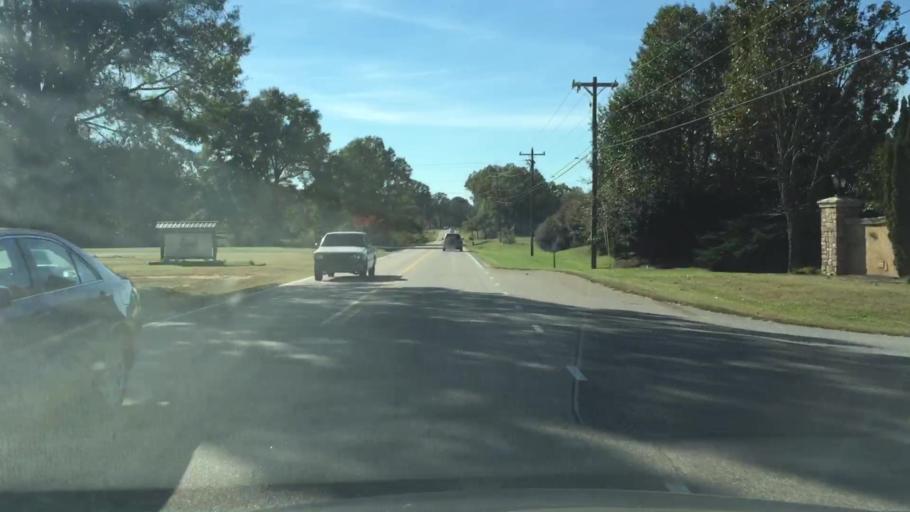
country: US
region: North Carolina
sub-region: Iredell County
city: Mooresville
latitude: 35.6185
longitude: -80.7328
